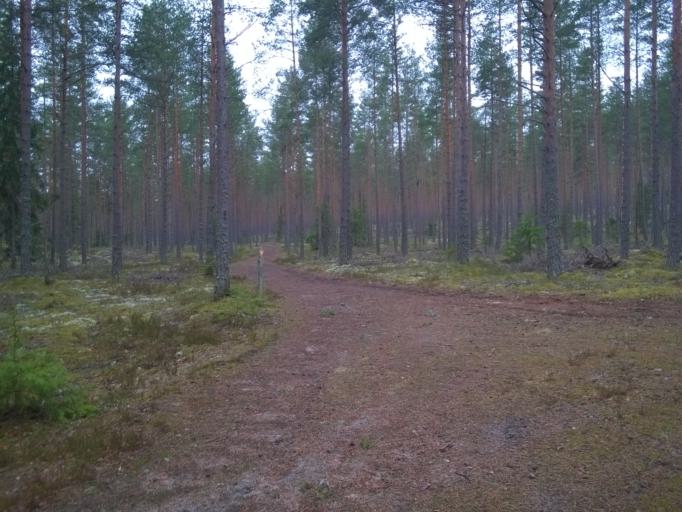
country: SE
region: Uppsala
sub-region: Osthammars Kommun
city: Bjorklinge
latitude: 60.1546
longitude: 17.5019
